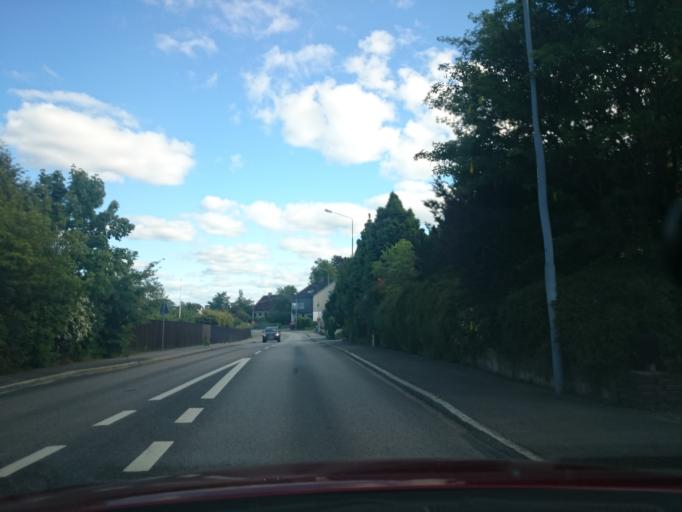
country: SE
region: Vaestra Goetaland
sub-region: Molndal
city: Moelndal
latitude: 57.6639
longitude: 12.0319
